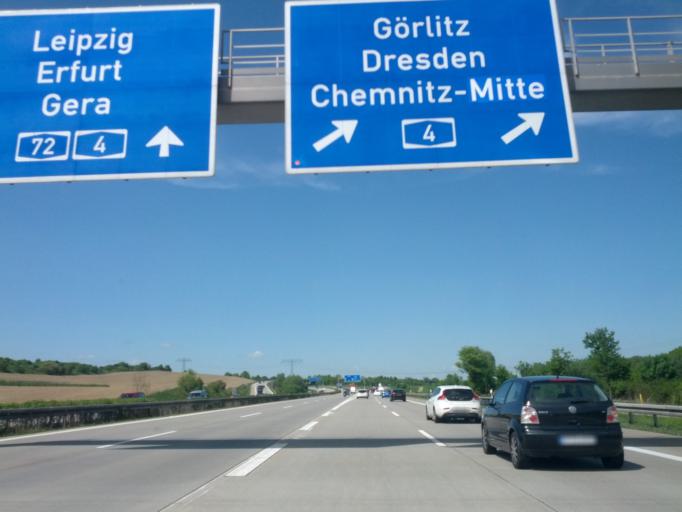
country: DE
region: Saxony
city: Wittgensdorf
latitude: 50.8422
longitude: 12.8457
